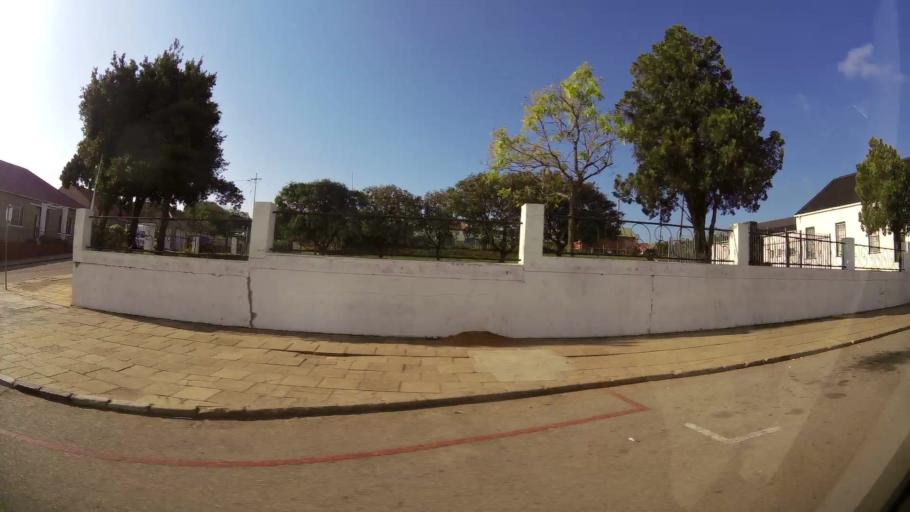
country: ZA
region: Eastern Cape
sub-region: Nelson Mandela Bay Metropolitan Municipality
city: Uitenhage
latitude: -33.7693
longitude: 25.4039
